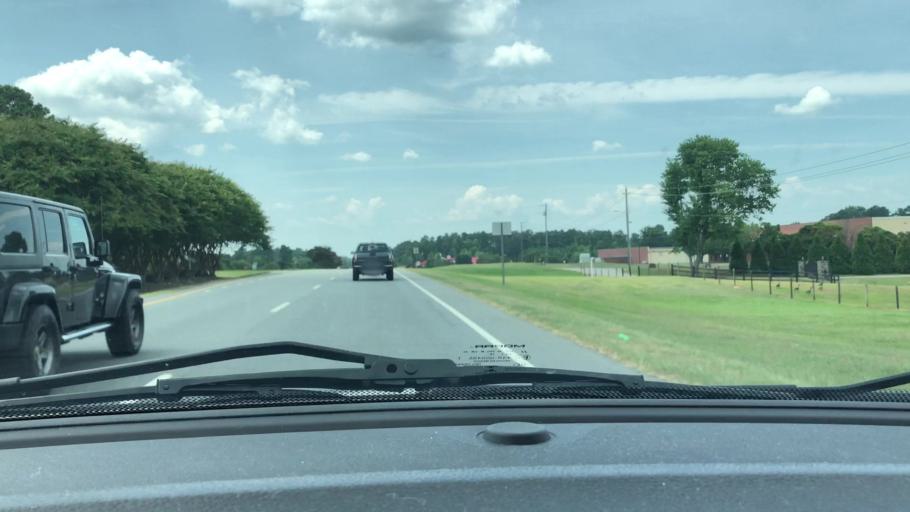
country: US
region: North Carolina
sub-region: Chatham County
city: Farmville
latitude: 35.5202
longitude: -79.2210
